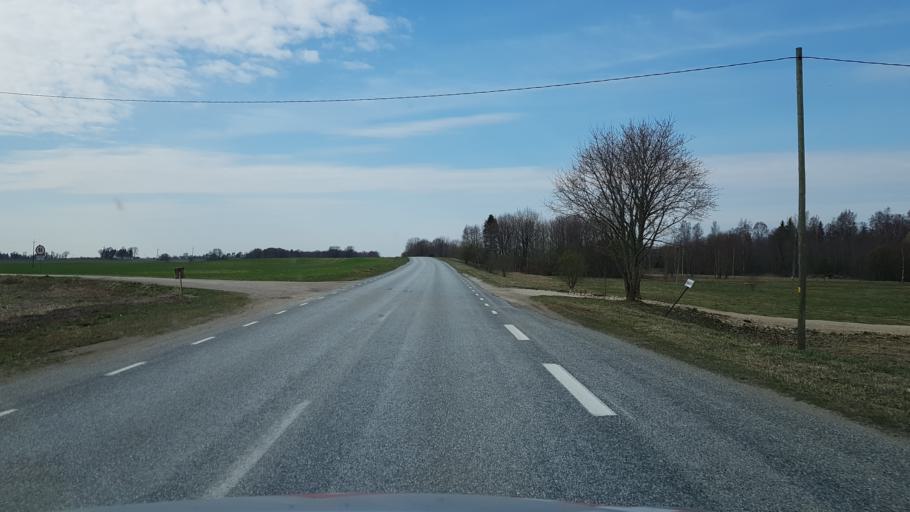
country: EE
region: Laeaene-Virumaa
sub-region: Haljala vald
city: Haljala
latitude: 59.4710
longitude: 26.1739
